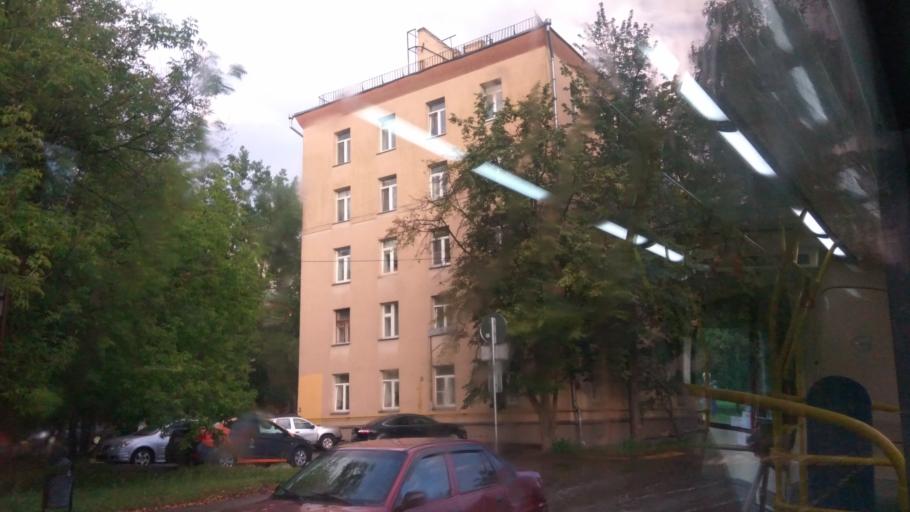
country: RU
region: Moskovskaya
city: Marfino
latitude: 55.7195
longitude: 37.3947
